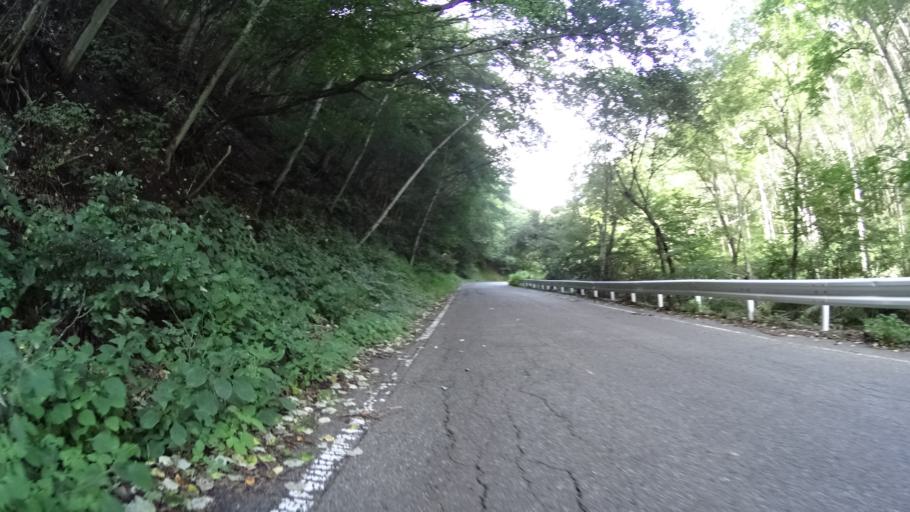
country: JP
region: Yamanashi
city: Nirasaki
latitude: 35.9079
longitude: 138.5399
